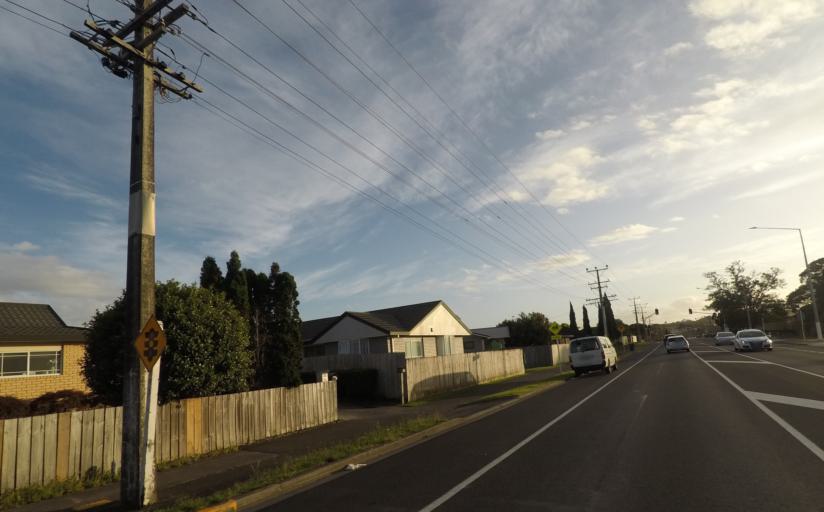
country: NZ
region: Auckland
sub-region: Auckland
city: Rosebank
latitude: -36.8045
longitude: 174.6382
